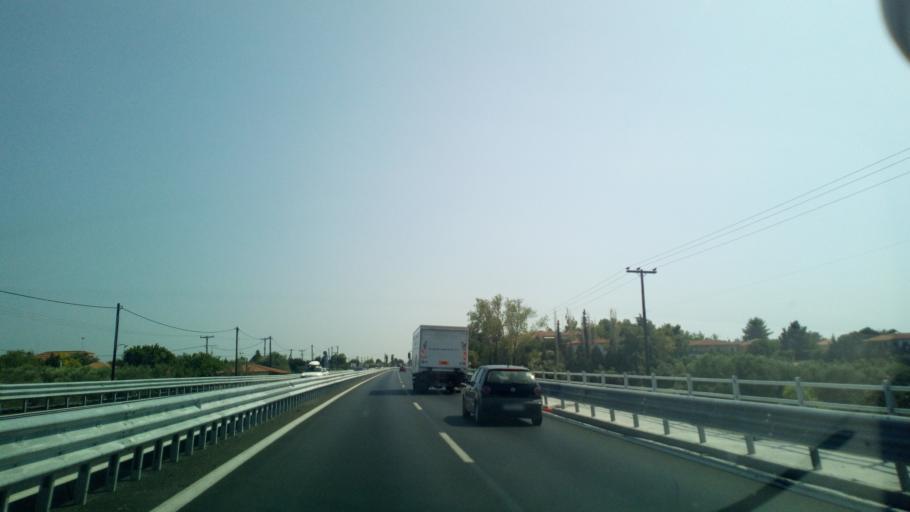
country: GR
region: Central Macedonia
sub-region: Nomos Chalkidikis
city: Nea Potidhaia
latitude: 40.2164
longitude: 23.3206
